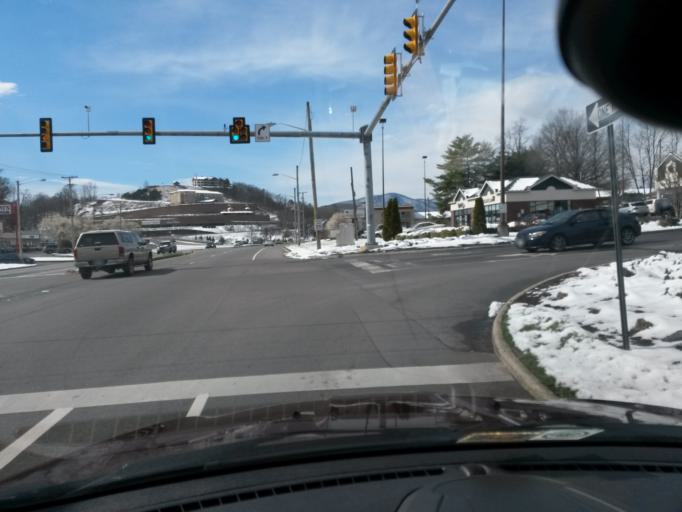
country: US
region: Virginia
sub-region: Roanoke County
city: Narrows
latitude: 37.2347
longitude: -79.9708
